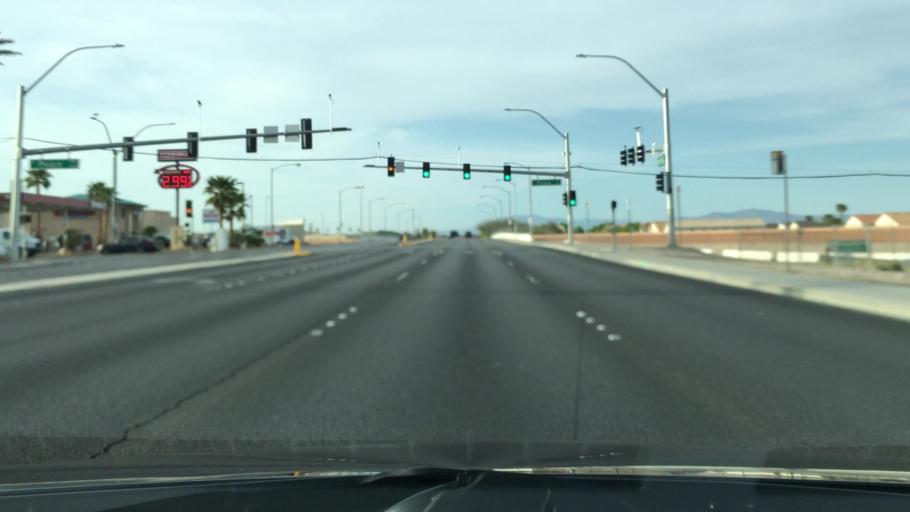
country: US
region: Nevada
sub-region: Clark County
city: Summerlin South
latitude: 36.1070
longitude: -115.2971
